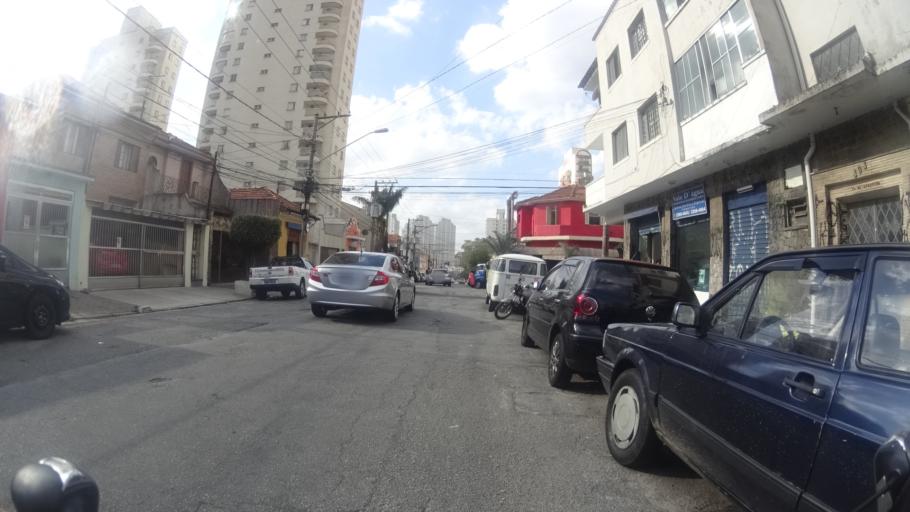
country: BR
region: Sao Paulo
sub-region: Sao Paulo
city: Sao Paulo
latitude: -23.5575
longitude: -46.5957
